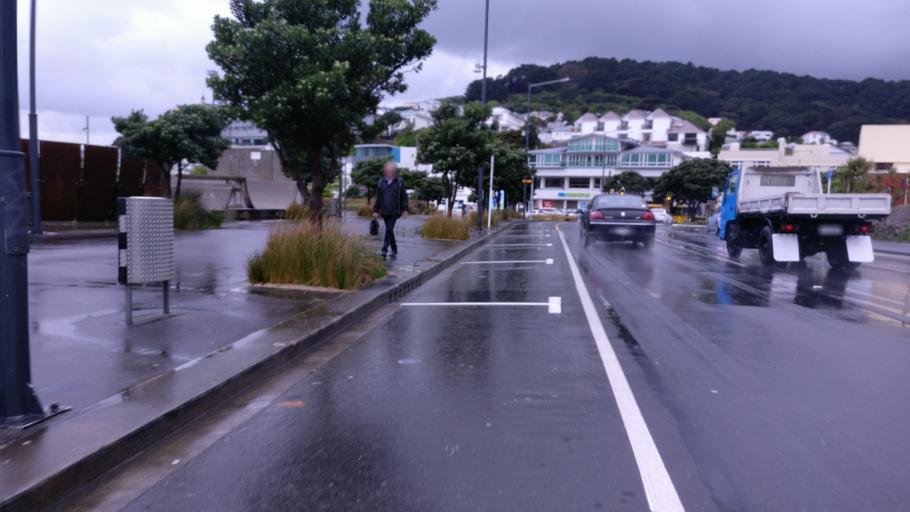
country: NZ
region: Wellington
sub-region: Wellington City
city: Wellington
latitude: -41.2920
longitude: 174.7844
